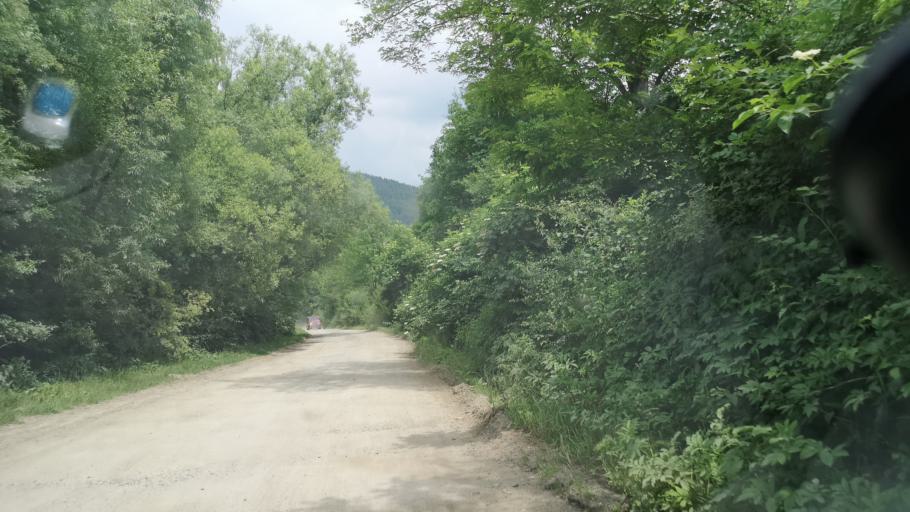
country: SK
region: Zilinsky
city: Ruzomberok
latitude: 49.1291
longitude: 19.4179
